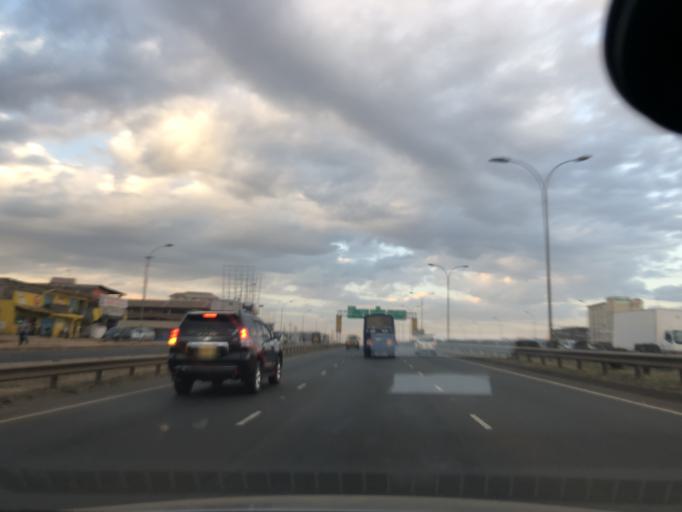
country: KE
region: Kiambu
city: Kiambu
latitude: -1.2074
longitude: 36.9135
